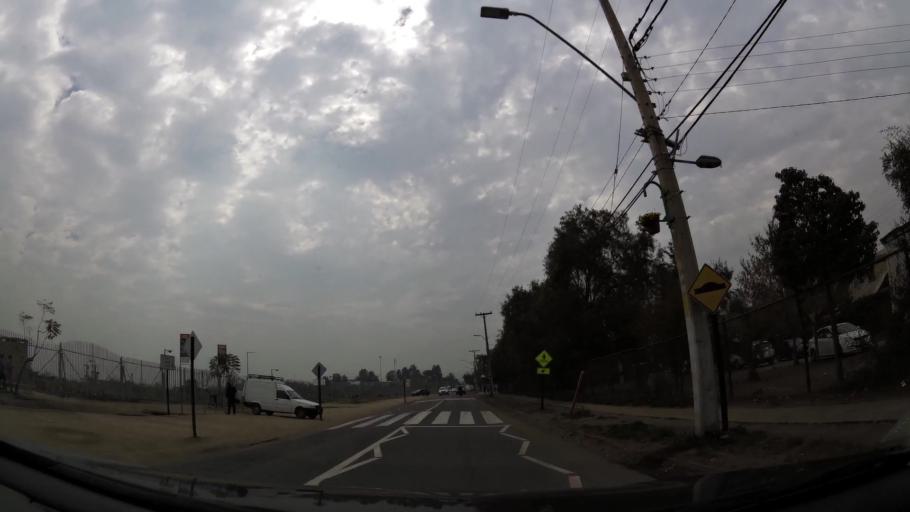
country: CL
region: Santiago Metropolitan
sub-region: Provincia de Chacabuco
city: Chicureo Abajo
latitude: -33.2080
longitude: -70.6845
